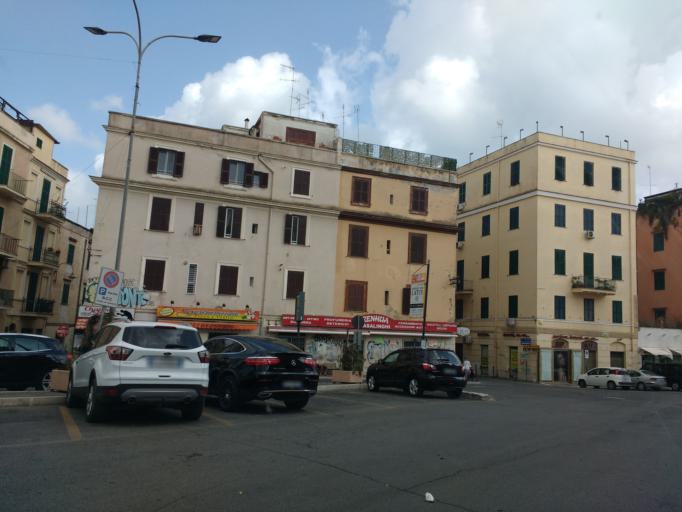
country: IT
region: Latium
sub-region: Citta metropolitana di Roma Capitale
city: Anzio
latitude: 41.4486
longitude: 12.6292
